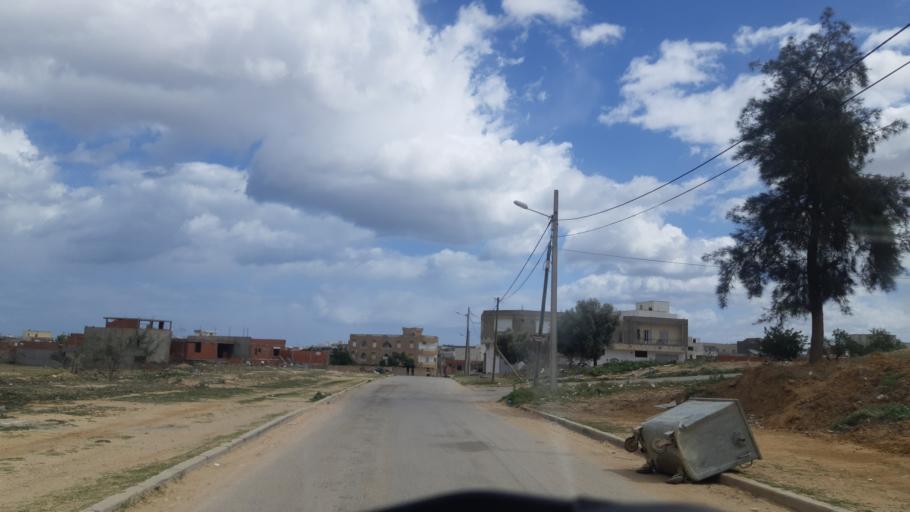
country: TN
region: Susah
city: Akouda
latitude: 35.8632
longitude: 10.5337
